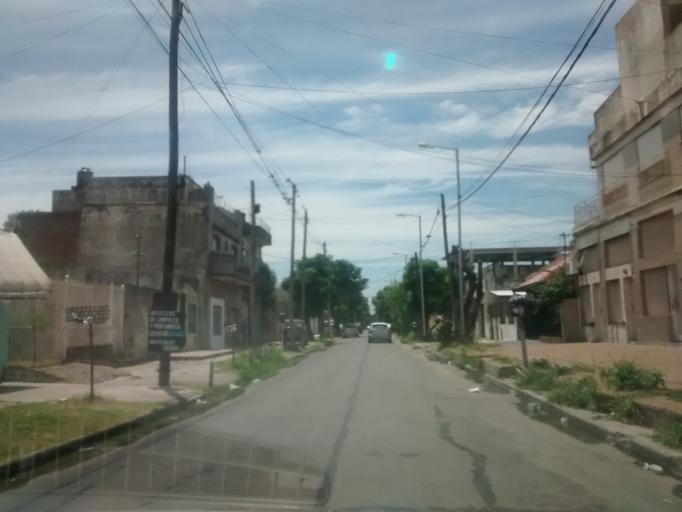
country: AR
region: Buenos Aires
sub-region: Partido de Avellaneda
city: Avellaneda
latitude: -34.6918
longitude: -58.3225
